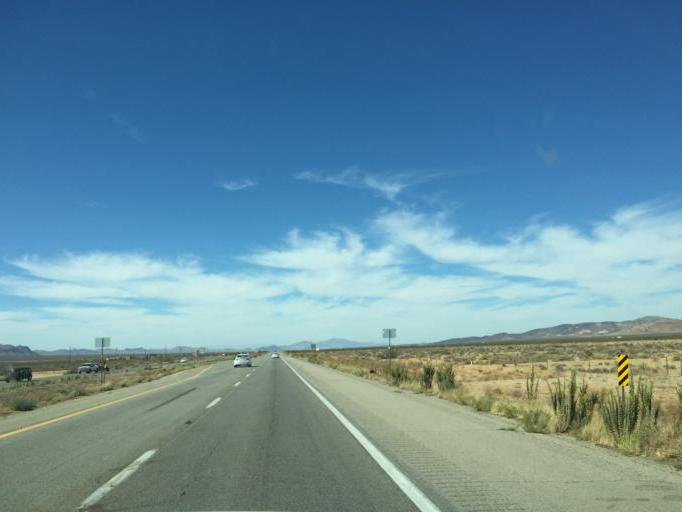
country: US
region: Arizona
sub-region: Mohave County
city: Dolan Springs
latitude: 35.5598
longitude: -114.3731
